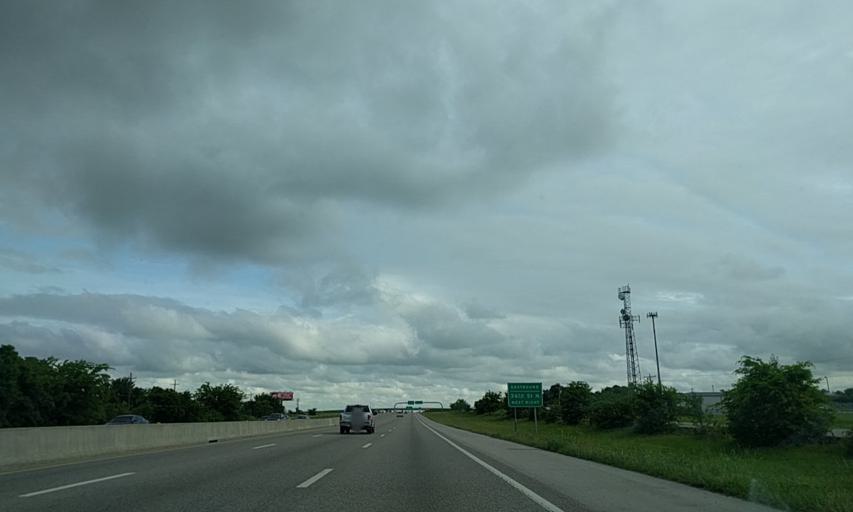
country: US
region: Oklahoma
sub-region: Tulsa County
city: Owasso
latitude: 36.1982
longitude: -95.8515
